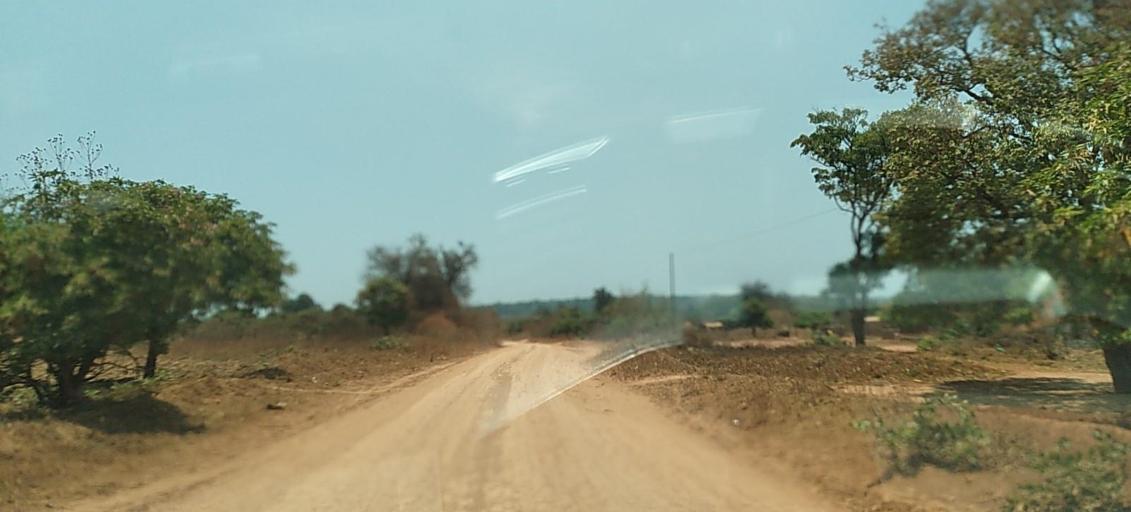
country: CD
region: Katanga
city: Kipushi
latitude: -11.7800
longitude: 27.1888
